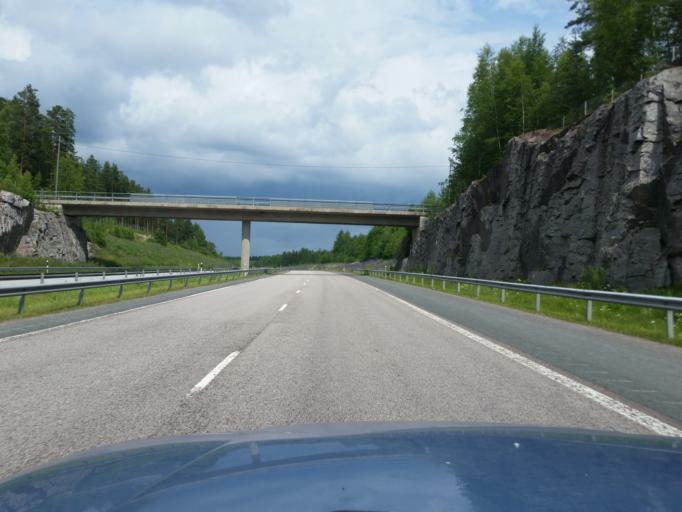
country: FI
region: Paijanne Tavastia
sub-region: Lahti
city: Nastola
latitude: 61.0097
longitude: 25.8165
